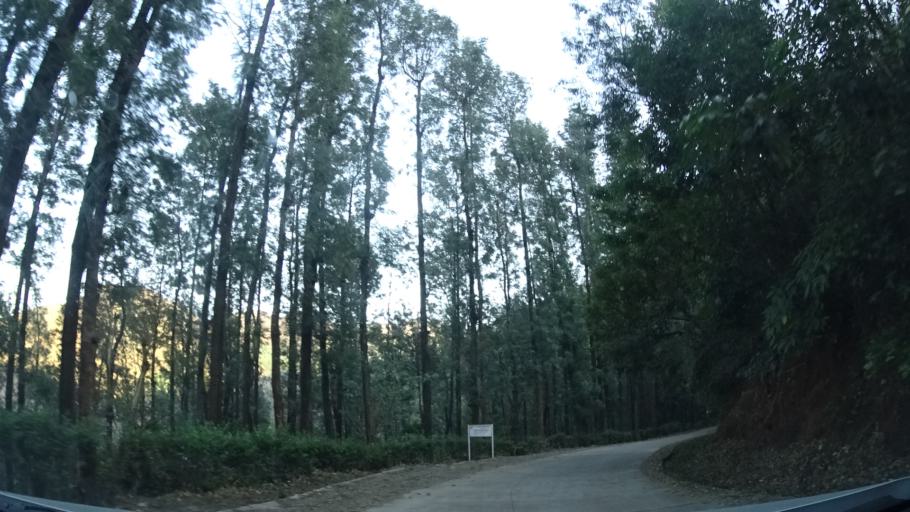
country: IN
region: Karnataka
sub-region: Chikmagalur
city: Tarikere
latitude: 13.5565
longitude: 75.7519
